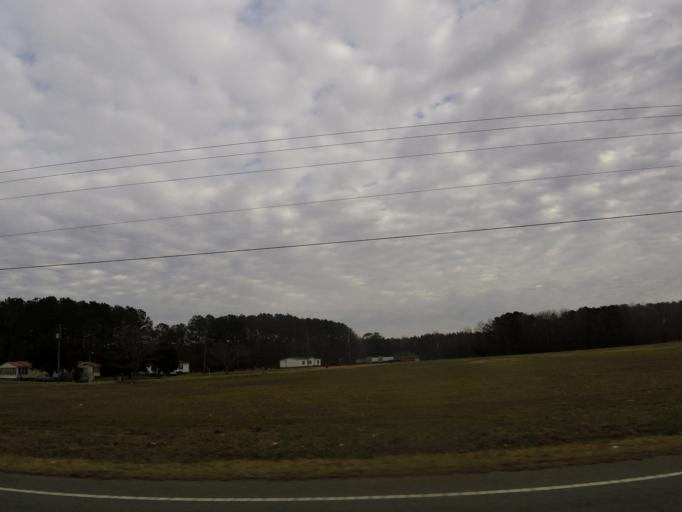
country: US
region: North Carolina
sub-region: Northampton County
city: Jackson
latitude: 36.3029
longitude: -77.2672
